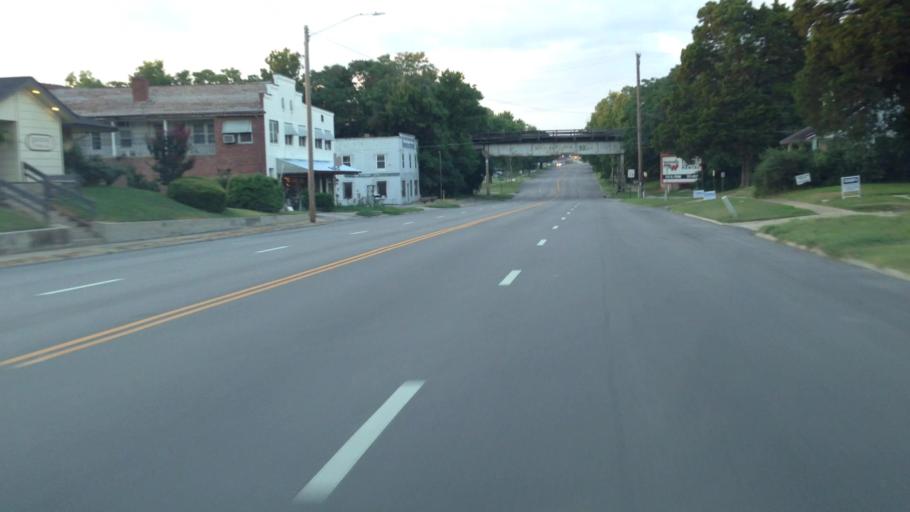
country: US
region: Kansas
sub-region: Montgomery County
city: Independence
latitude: 37.2312
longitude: -95.7065
